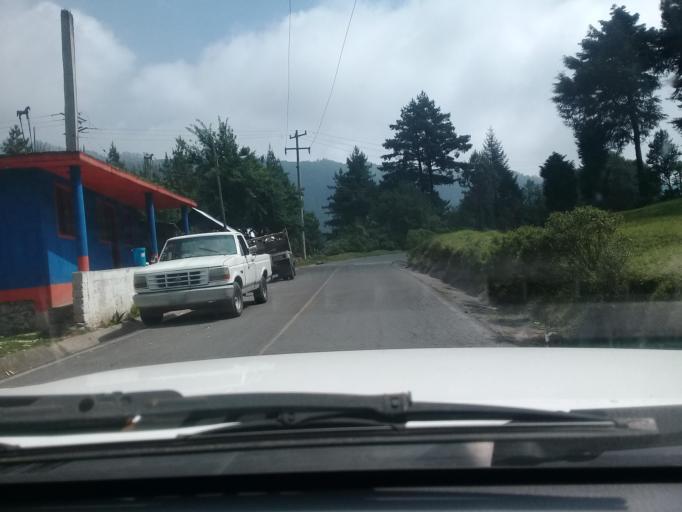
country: MX
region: Veracruz
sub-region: Mariano Escobedo
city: Texmola
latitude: 18.9460
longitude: -97.2213
